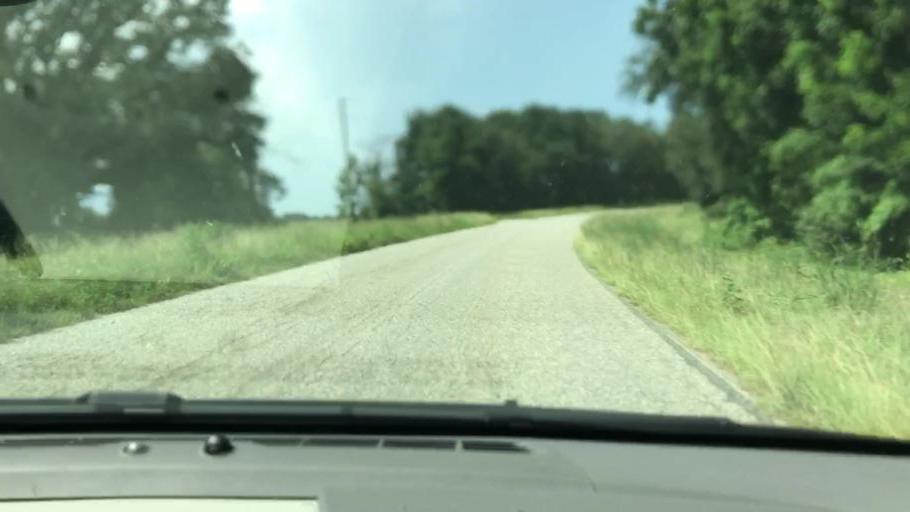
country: US
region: Georgia
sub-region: Seminole County
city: Donalsonville
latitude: 31.1657
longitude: -85.0016
